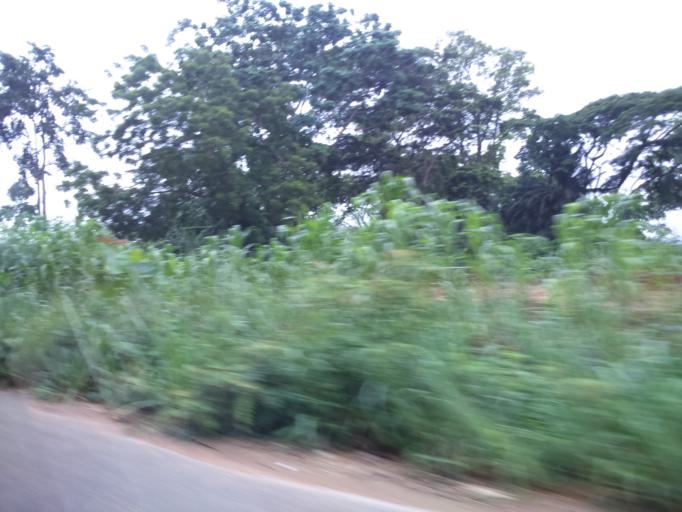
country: CI
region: Moyen-Comoe
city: Abengourou
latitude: 6.6549
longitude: -3.2876
